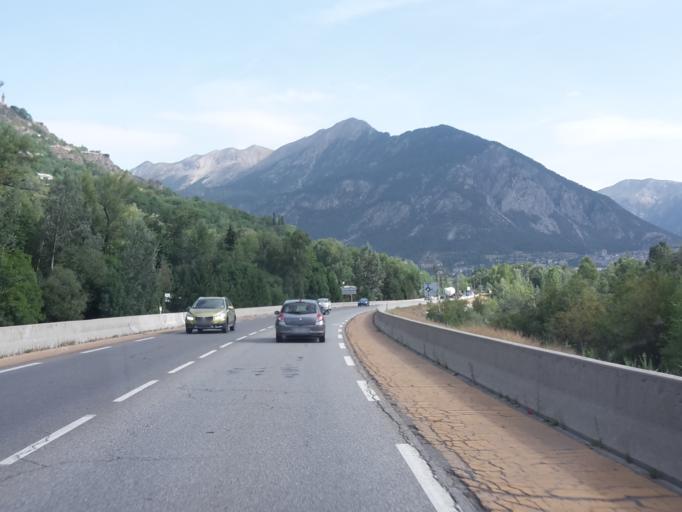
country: FR
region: Provence-Alpes-Cote d'Azur
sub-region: Departement des Hautes-Alpes
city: Villar-Saint-Pancrace
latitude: 44.8779
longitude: 6.6182
